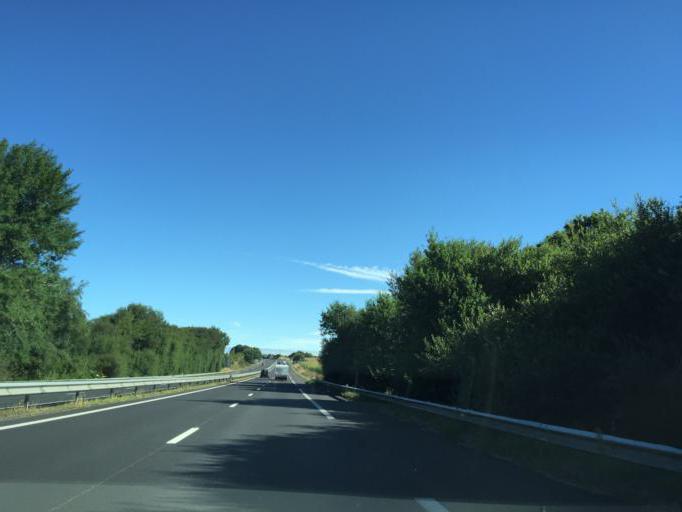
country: FR
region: Brittany
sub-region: Departement des Cotes-d'Armor
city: Saint-Samson-sur-Rance
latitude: 48.4978
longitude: -2.0403
